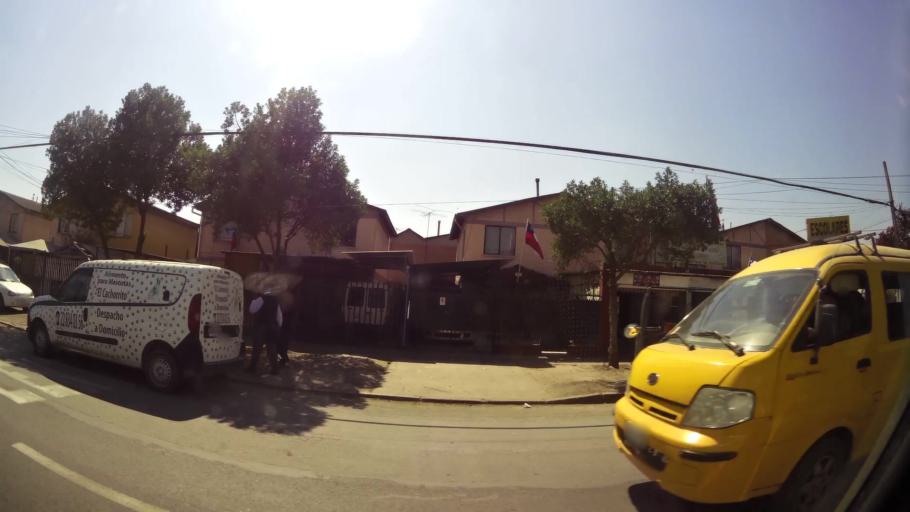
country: CL
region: Santiago Metropolitan
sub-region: Provincia de Talagante
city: Penaflor
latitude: -33.5746
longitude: -70.8156
